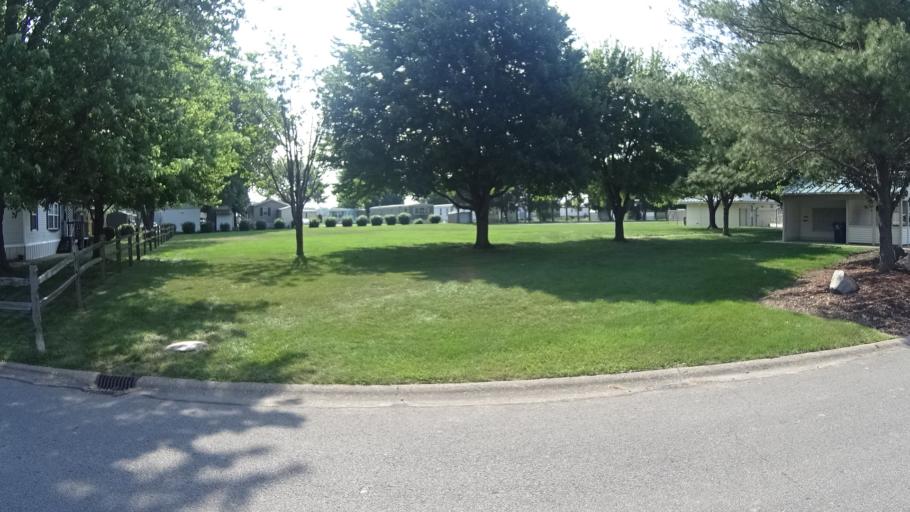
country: US
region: Ohio
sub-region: Lorain County
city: Vermilion
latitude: 41.3932
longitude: -82.4299
